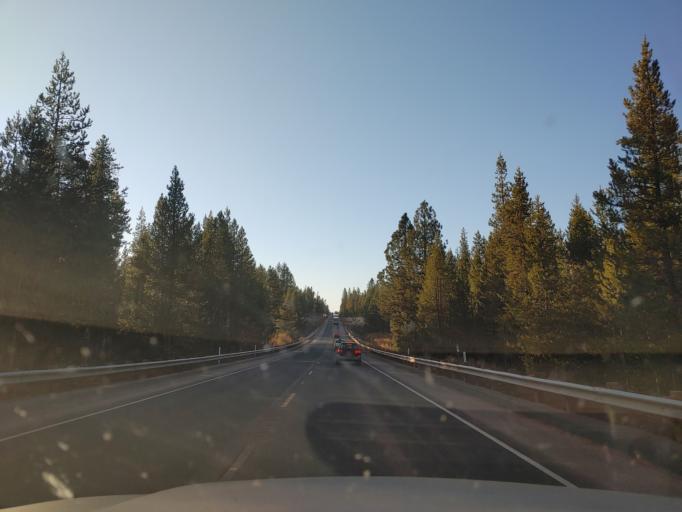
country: US
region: Oregon
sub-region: Deschutes County
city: La Pine
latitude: 43.3788
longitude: -121.7995
